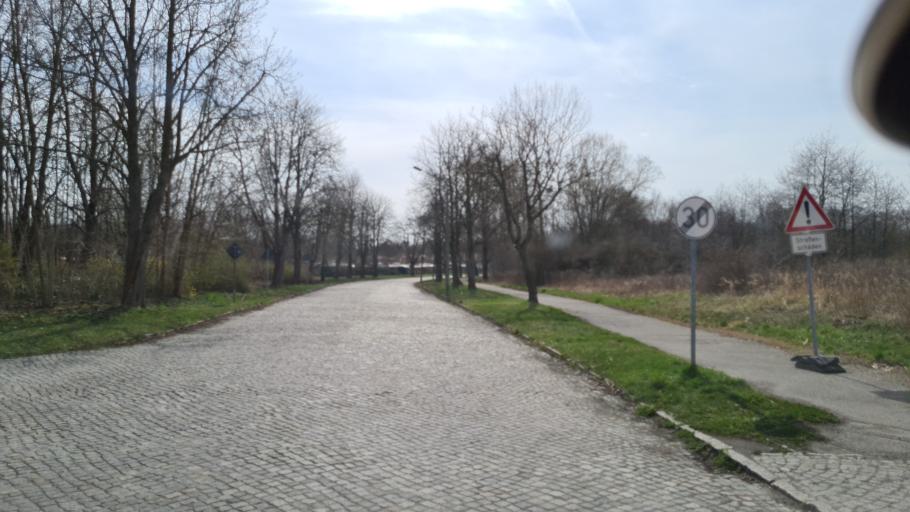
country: DE
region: Brandenburg
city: Lauchhammer
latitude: 51.4977
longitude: 13.7453
